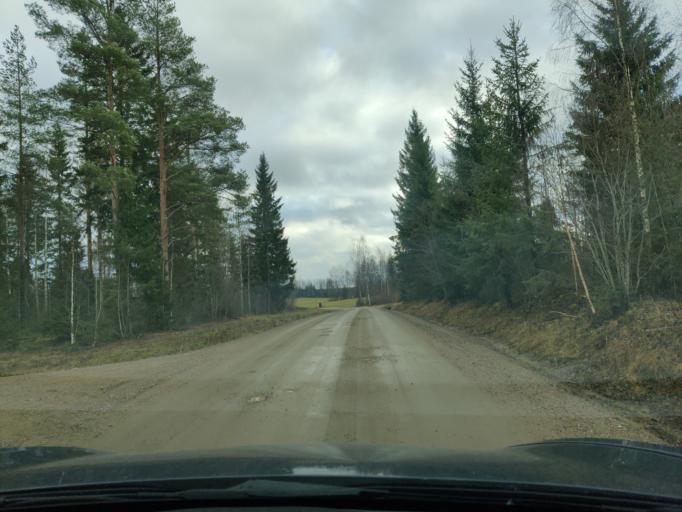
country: FI
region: Northern Savo
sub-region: Ylae-Savo
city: Kiuruvesi
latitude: 63.6381
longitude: 26.6464
